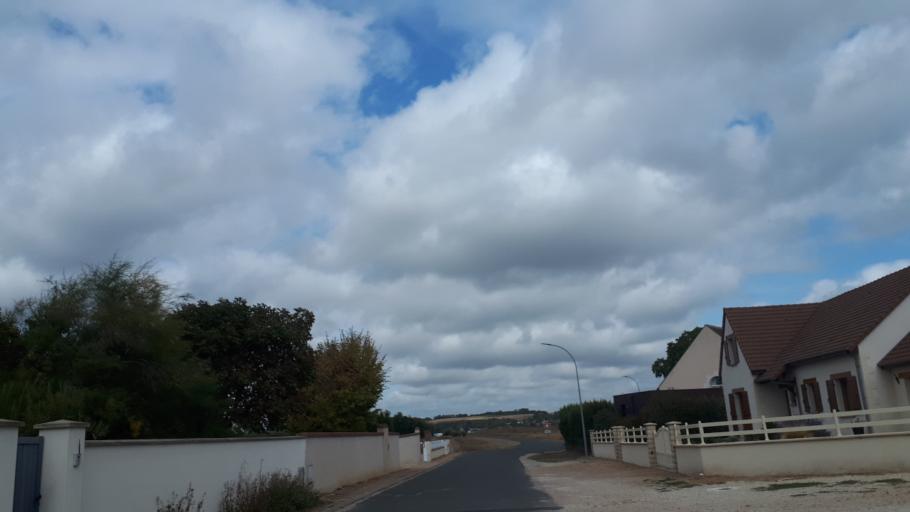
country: FR
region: Centre
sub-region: Departement du Loir-et-Cher
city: Villiers-sur-Loir
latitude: 47.7933
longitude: 0.9969
